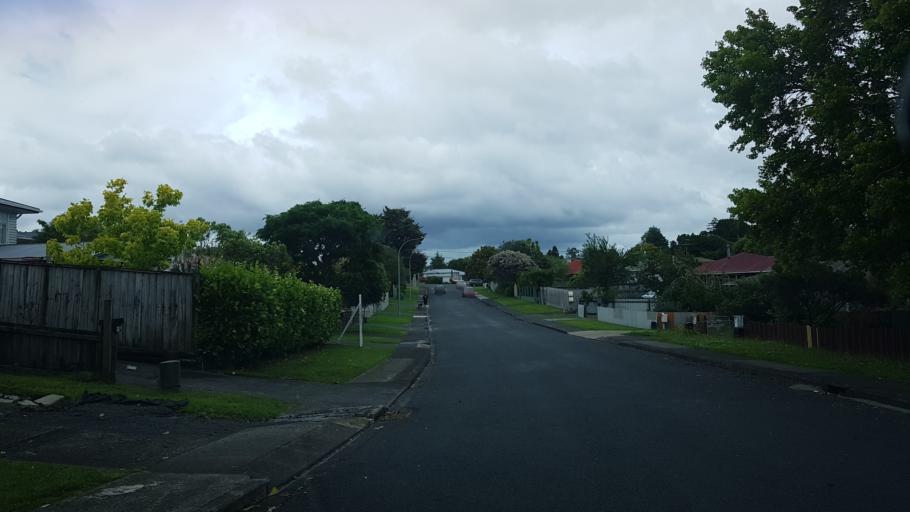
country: NZ
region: Auckland
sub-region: Auckland
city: Rosebank
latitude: -36.8298
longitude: 174.6539
